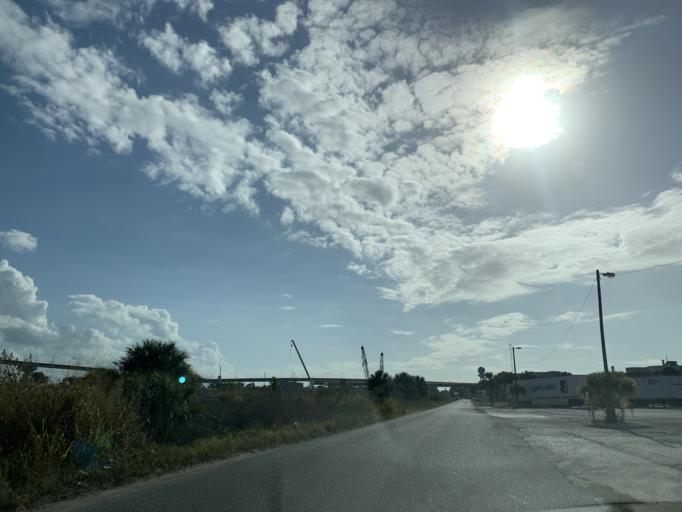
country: US
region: Florida
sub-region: Hillsborough County
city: Tampa
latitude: 27.8972
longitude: -82.5077
